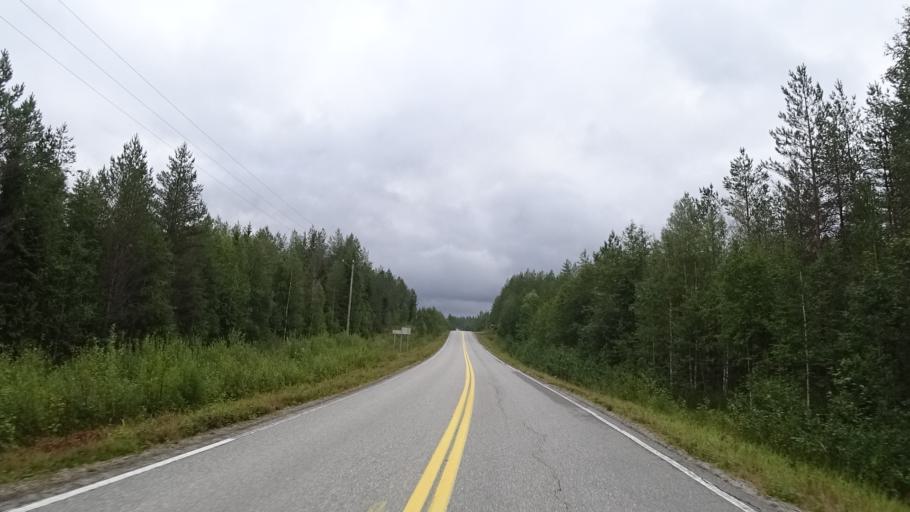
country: FI
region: North Karelia
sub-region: Joensuu
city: Ilomantsi
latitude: 63.2502
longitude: 30.7141
